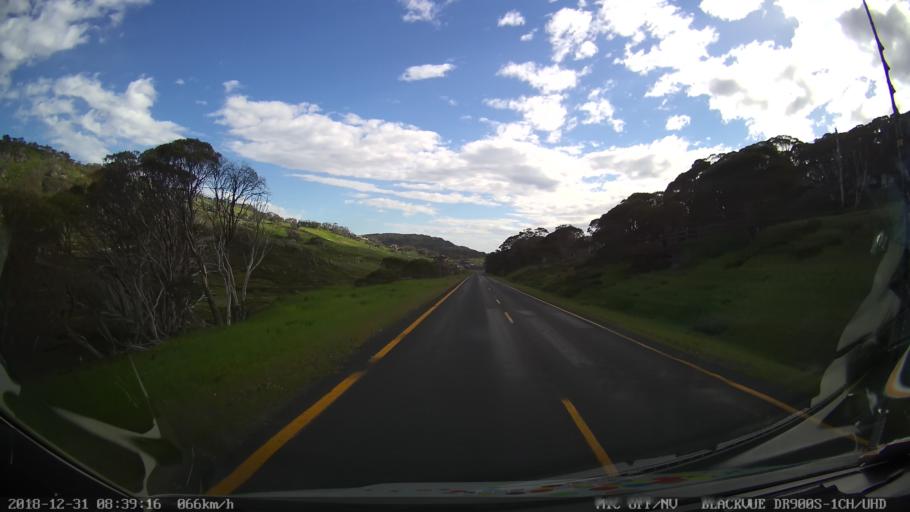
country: AU
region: New South Wales
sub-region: Snowy River
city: Jindabyne
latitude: -36.4103
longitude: 148.4043
